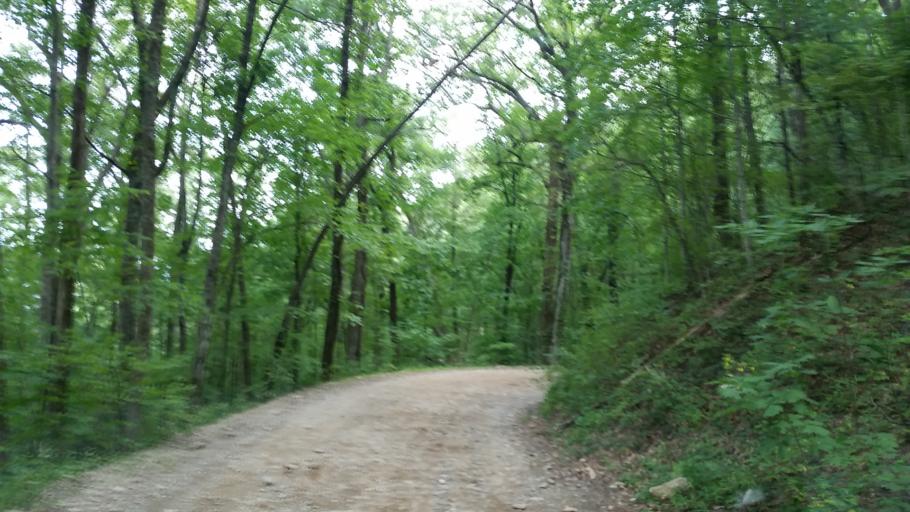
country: US
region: Georgia
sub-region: Lumpkin County
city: Dahlonega
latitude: 34.6509
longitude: -84.0855
